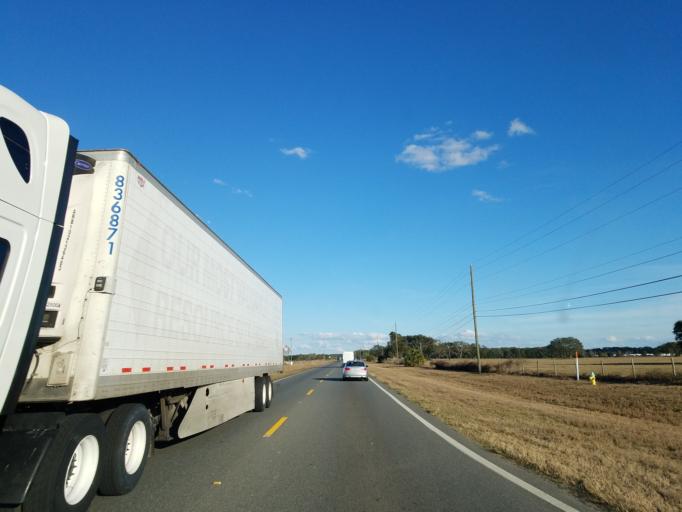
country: US
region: Florida
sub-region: Sumter County
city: Lake Panasoffkee
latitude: 28.7488
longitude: -82.0849
